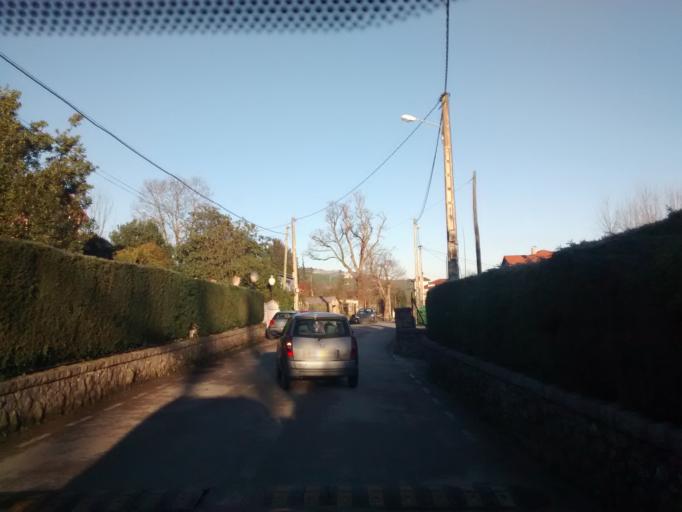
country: ES
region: Cantabria
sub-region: Provincia de Cantabria
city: Entrambasaguas
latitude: 43.3473
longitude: -3.7010
